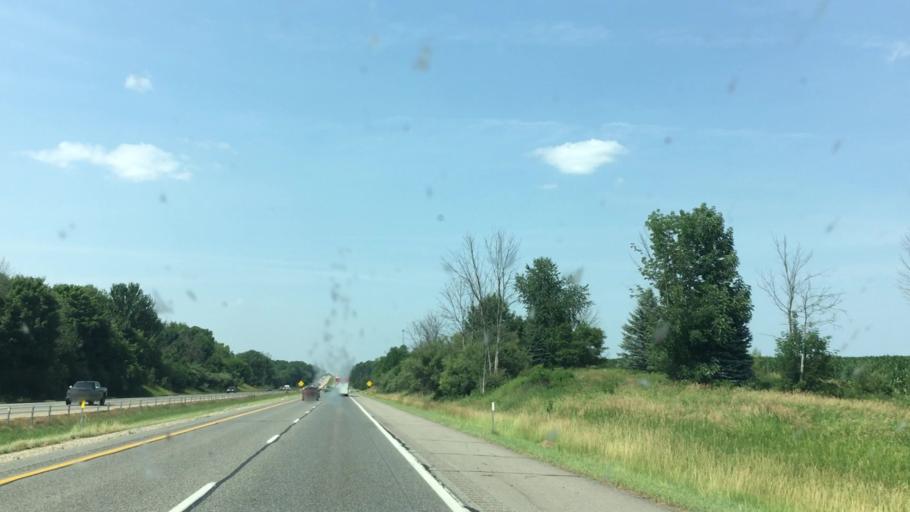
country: US
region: Michigan
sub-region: Allegan County
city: Otsego
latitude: 42.5615
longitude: -85.6622
